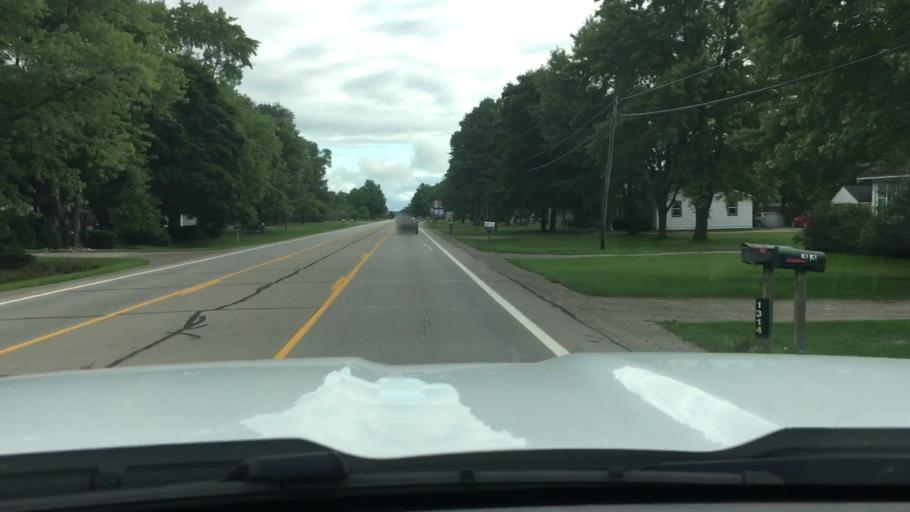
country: US
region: Michigan
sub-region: Tuscola County
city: Caro
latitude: 43.5049
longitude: -83.3752
